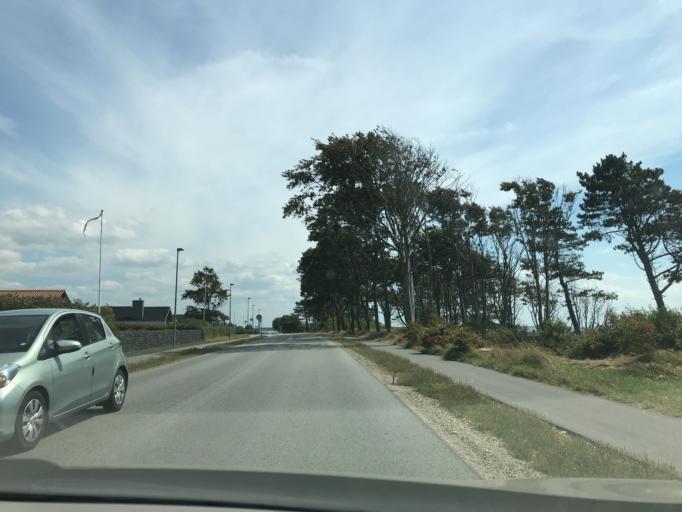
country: DK
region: Central Jutland
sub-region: Ringkobing-Skjern Kommune
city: Ringkobing
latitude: 56.0729
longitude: 8.2722
